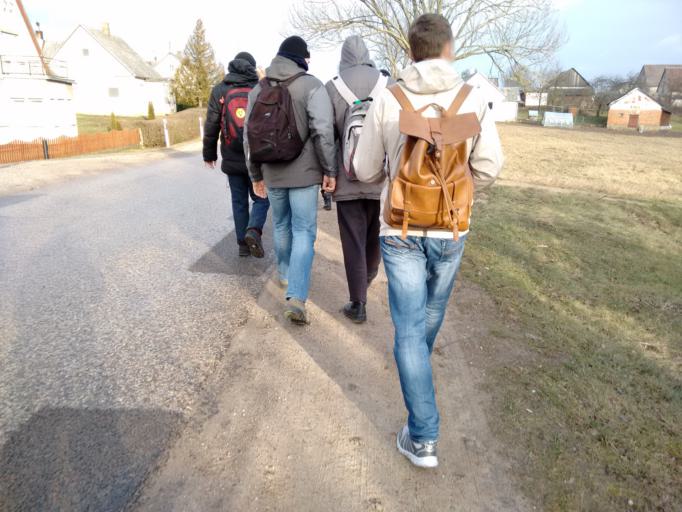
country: LT
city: Veisiejai
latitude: 54.2311
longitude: 23.8200
